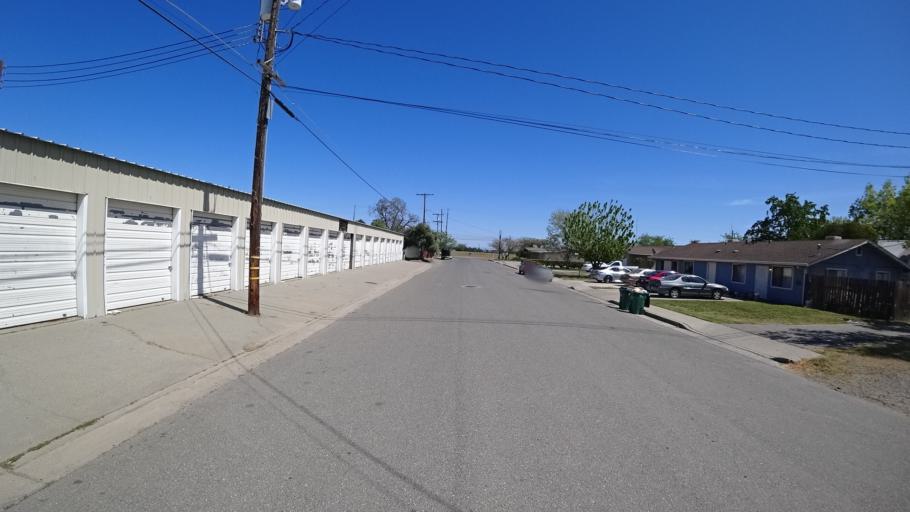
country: US
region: California
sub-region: Glenn County
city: Orland
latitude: 39.7464
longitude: -122.1795
